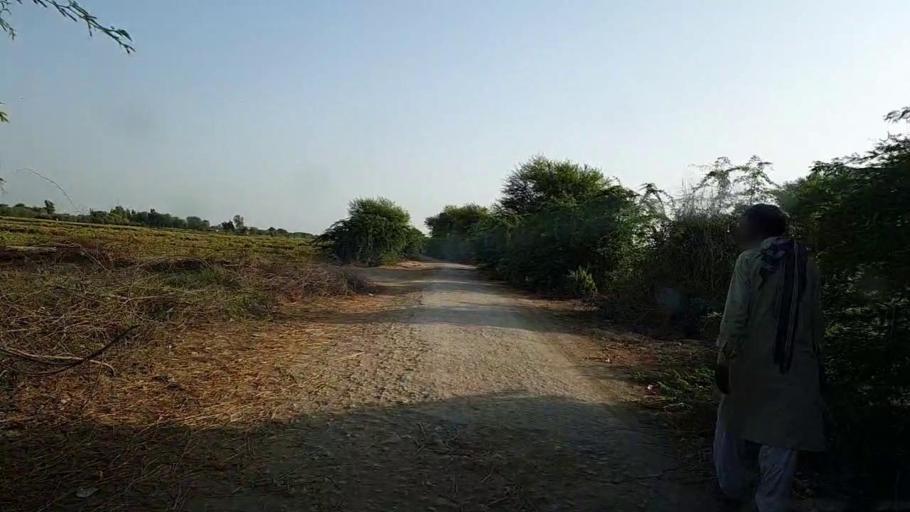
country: PK
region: Sindh
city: Bulri
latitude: 24.7478
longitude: 68.4219
